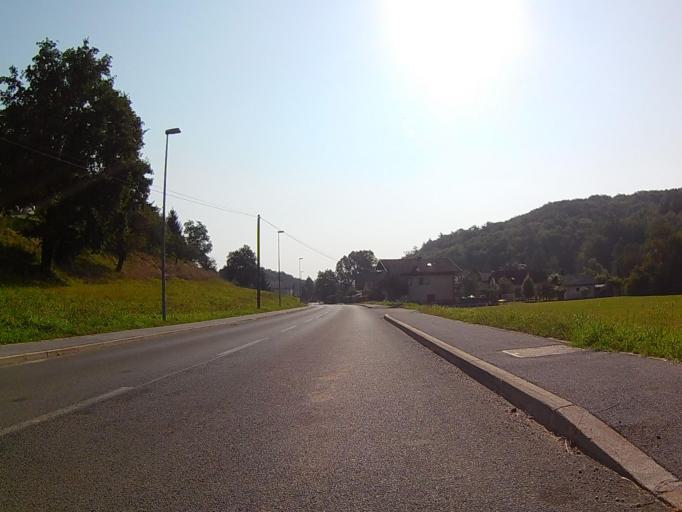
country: SI
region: Kungota
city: Zgornja Kungota
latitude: 46.6095
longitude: 15.6287
